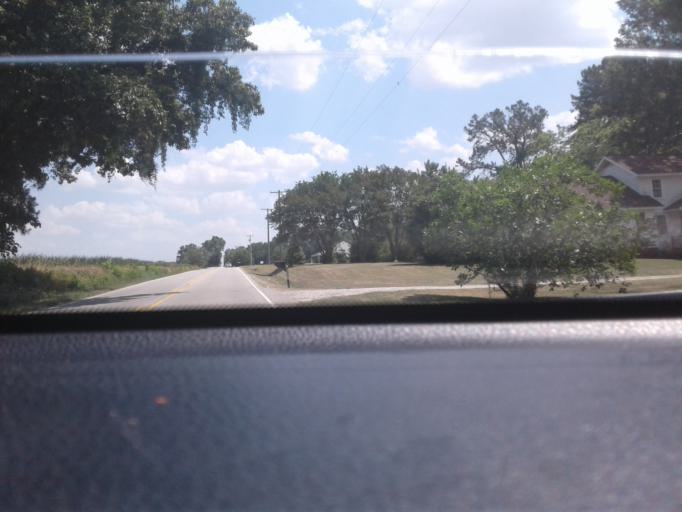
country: US
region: North Carolina
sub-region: Harnett County
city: Erwin
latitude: 35.2985
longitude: -78.6673
